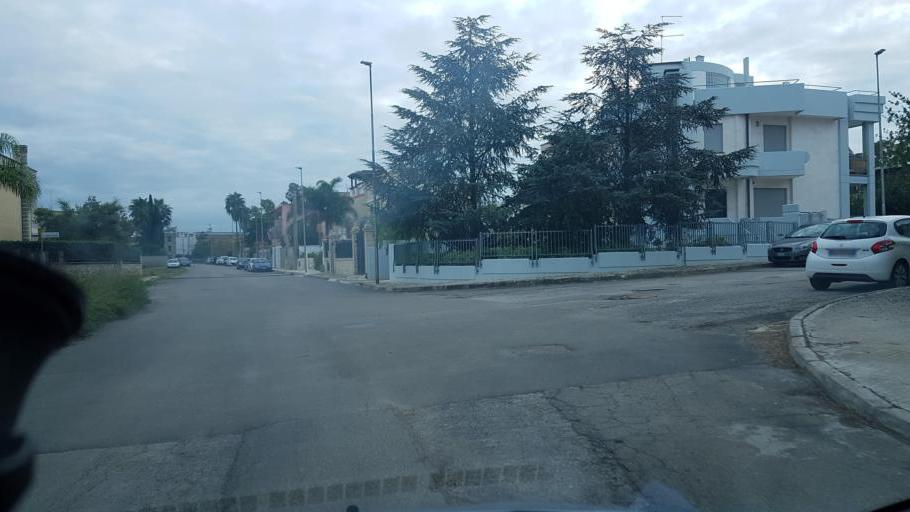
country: IT
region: Apulia
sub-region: Provincia di Brindisi
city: Oria
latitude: 40.5060
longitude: 17.6397
